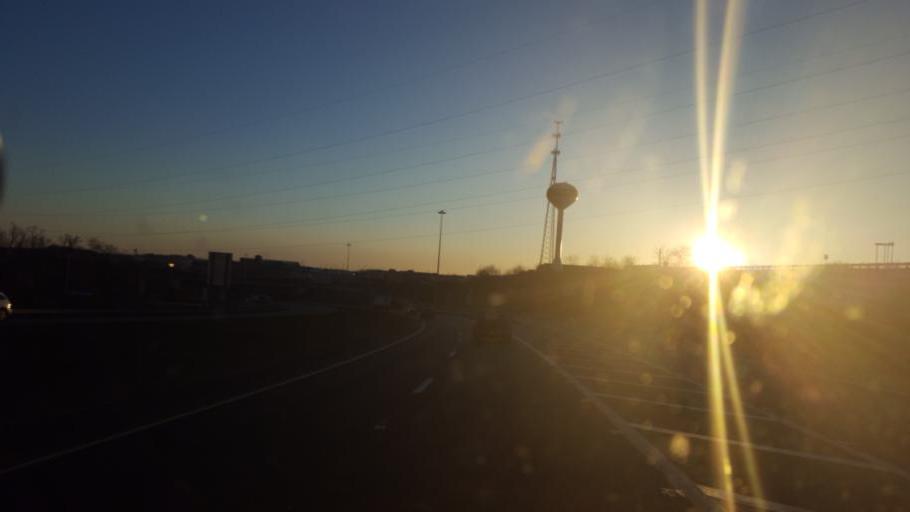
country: US
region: West Virginia
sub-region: Ohio County
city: Bethlehem
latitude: 40.0643
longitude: -80.5887
